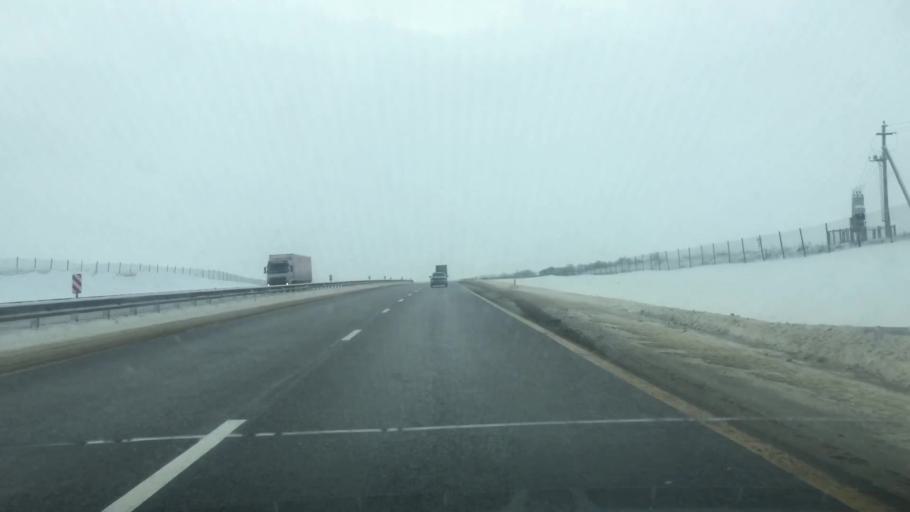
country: RU
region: Tula
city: Yefremov
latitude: 53.1342
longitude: 38.2374
